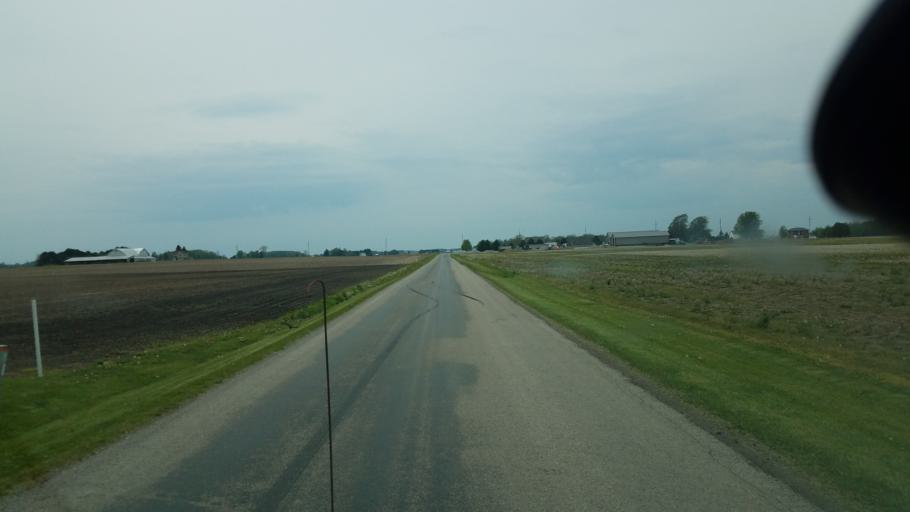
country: US
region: Ohio
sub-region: Richland County
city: Shelby
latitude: 40.8946
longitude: -82.6792
